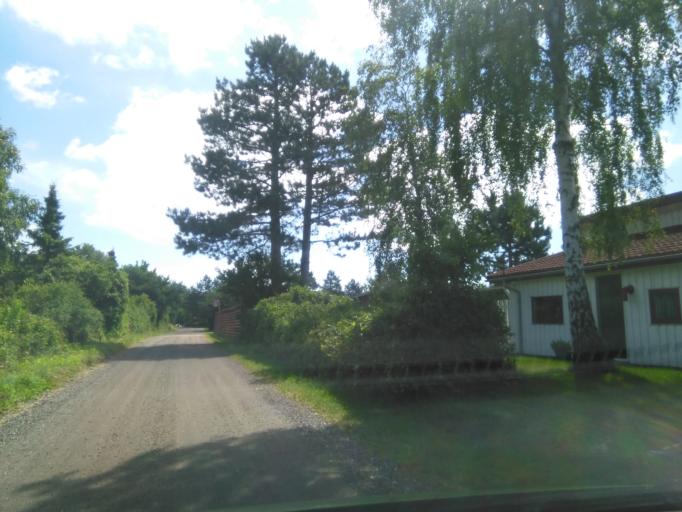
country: DK
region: Central Jutland
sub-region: Arhus Kommune
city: Logten
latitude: 56.1888
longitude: 10.3709
